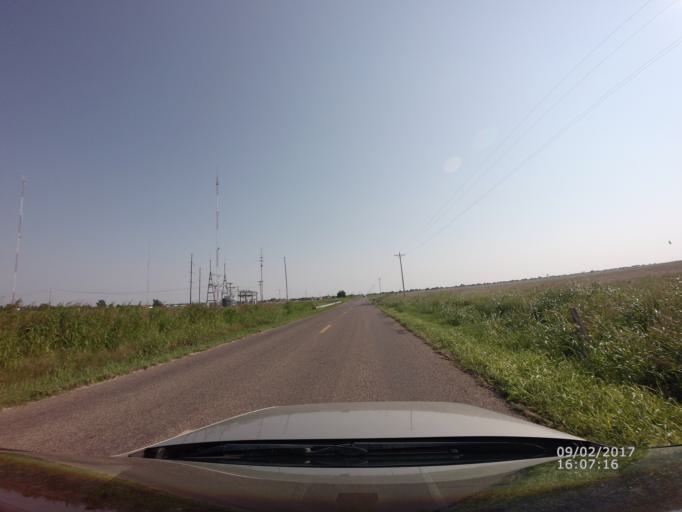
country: US
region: New Mexico
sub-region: Curry County
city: Clovis
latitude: 34.4418
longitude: -103.2141
